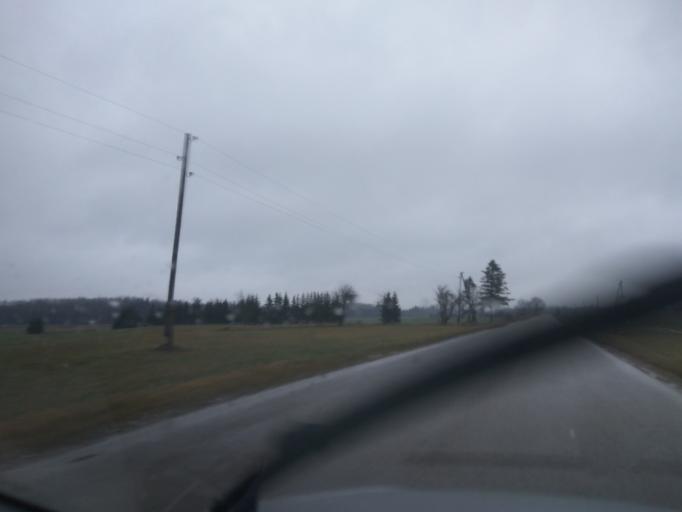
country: LV
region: Saldus Rajons
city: Saldus
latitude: 56.8384
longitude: 22.3788
